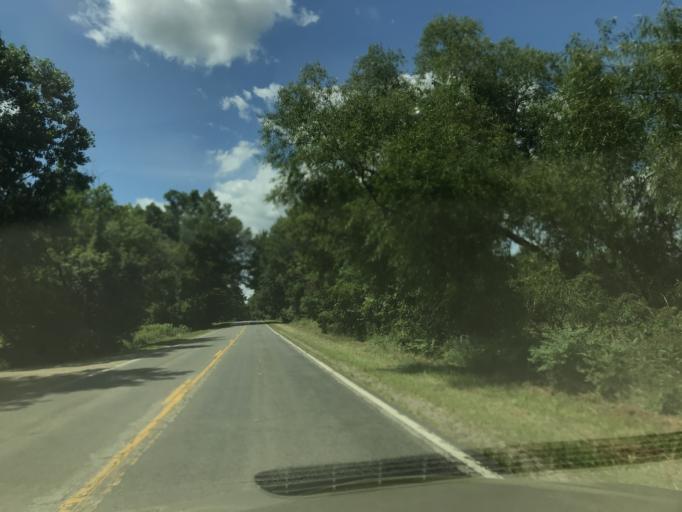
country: US
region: Michigan
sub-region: Ingham County
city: Leslie
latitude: 42.4511
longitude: -84.4903
